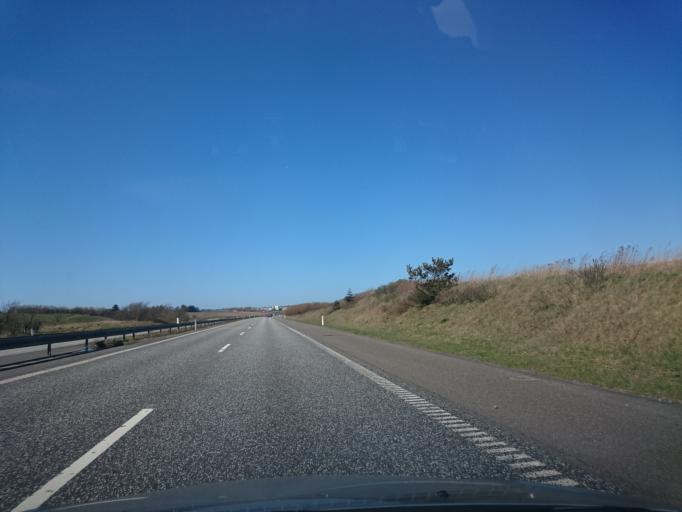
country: DK
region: North Denmark
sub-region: Hjorring Kommune
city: Hirtshals
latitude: 57.5347
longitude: 10.0099
